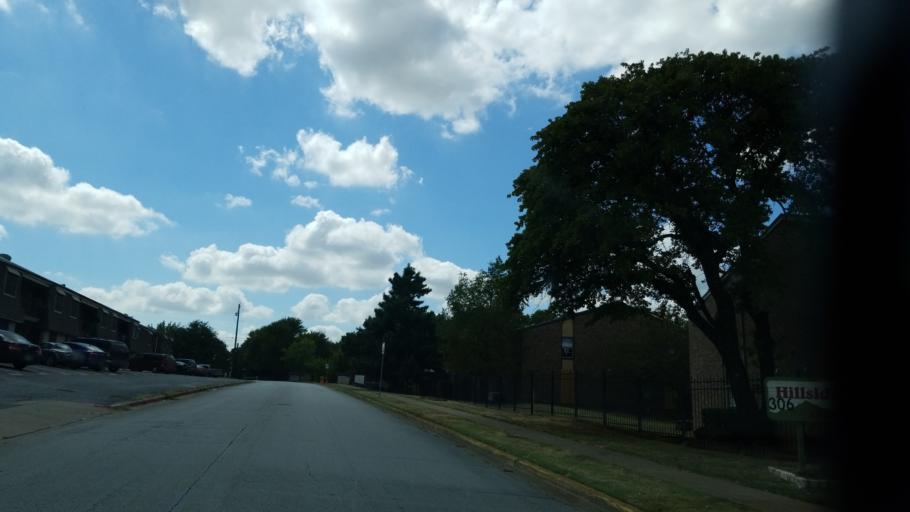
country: US
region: Texas
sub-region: Tarrant County
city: Euless
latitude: 32.8346
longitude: -97.0874
